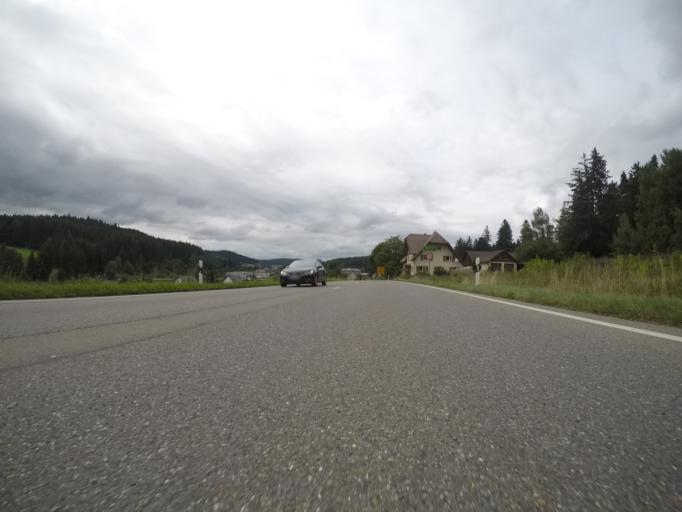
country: DE
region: Baden-Wuerttemberg
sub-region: Freiburg Region
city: Konigsfeld im Schwarzwald
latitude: 48.1191
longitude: 8.3956
